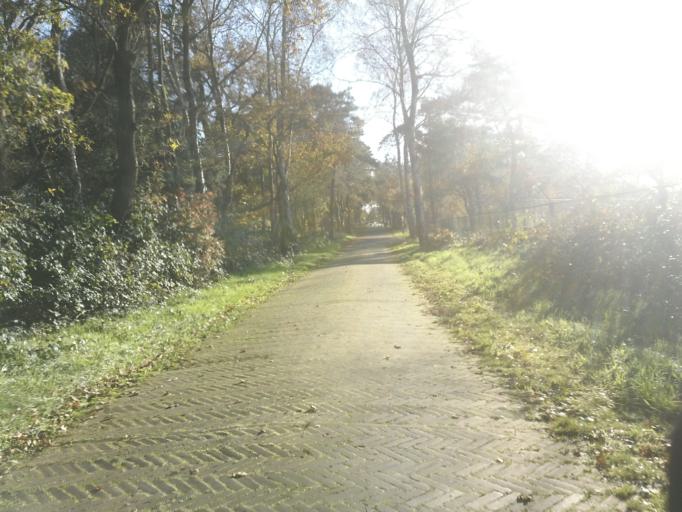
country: NL
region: Utrecht
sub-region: Gemeente Soest
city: Soest
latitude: 52.1355
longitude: 5.2780
